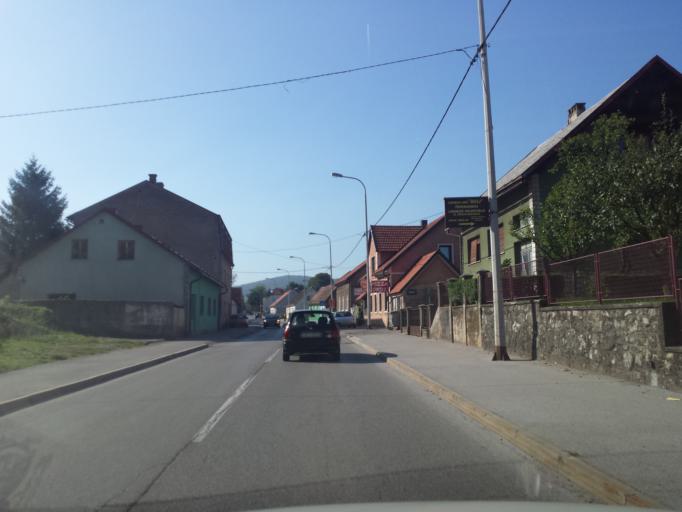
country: HR
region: Karlovacka
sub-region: Grad Ogulin
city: Ogulin
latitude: 45.2623
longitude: 15.2321
